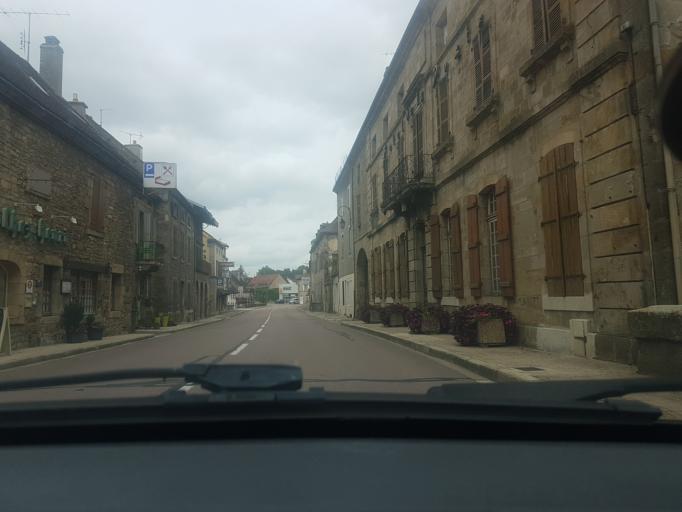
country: FR
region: Bourgogne
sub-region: Departement de la Cote-d'Or
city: Arnay-le-Duc
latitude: 47.1346
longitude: 4.4857
